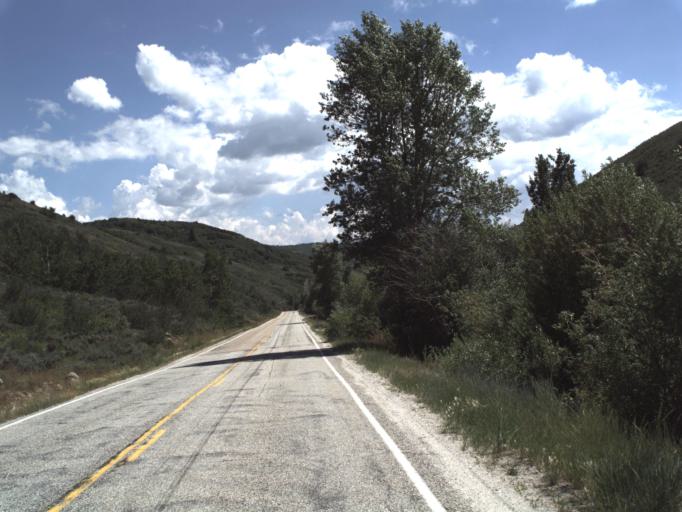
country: US
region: Utah
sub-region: Weber County
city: Wolf Creek
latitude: 41.3825
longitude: -111.5926
